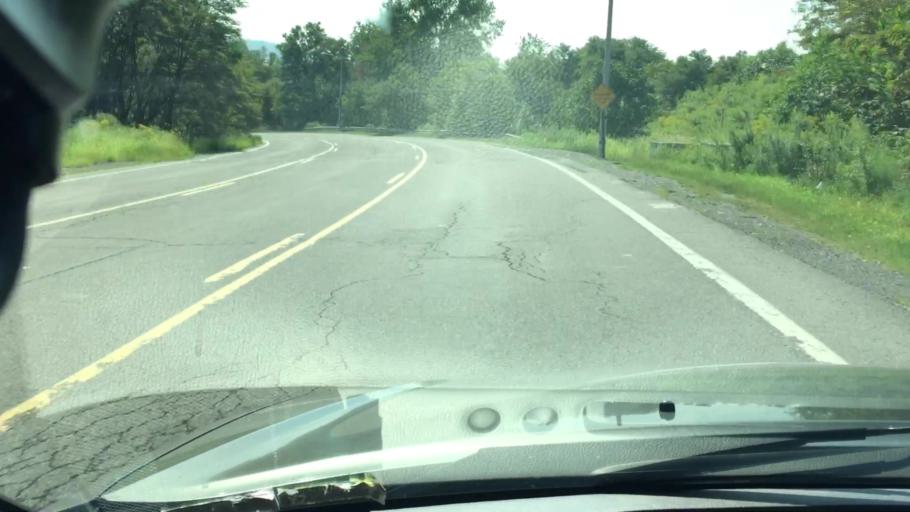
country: US
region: Pennsylvania
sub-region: Luzerne County
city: Plymouth
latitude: 41.1993
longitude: -75.9411
